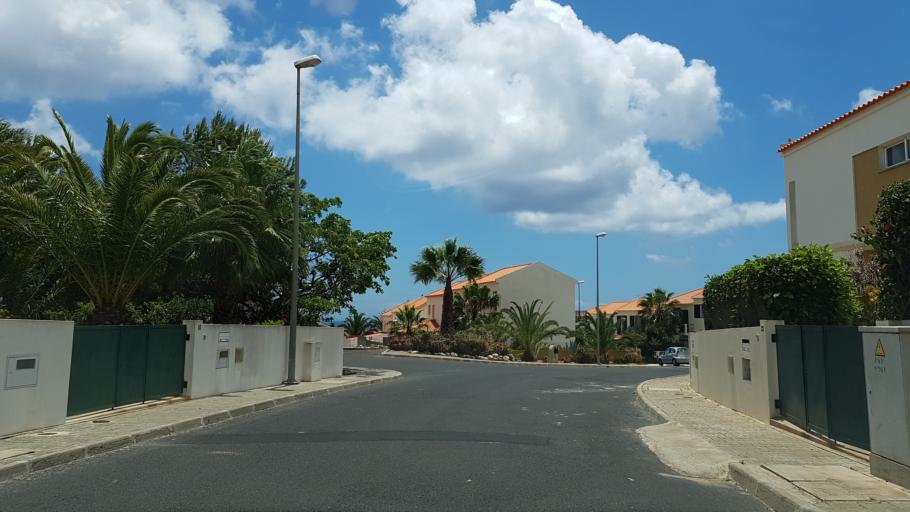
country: PT
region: Madeira
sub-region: Porto Santo
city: Vila de Porto Santo
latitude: 33.0622
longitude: -16.3538
